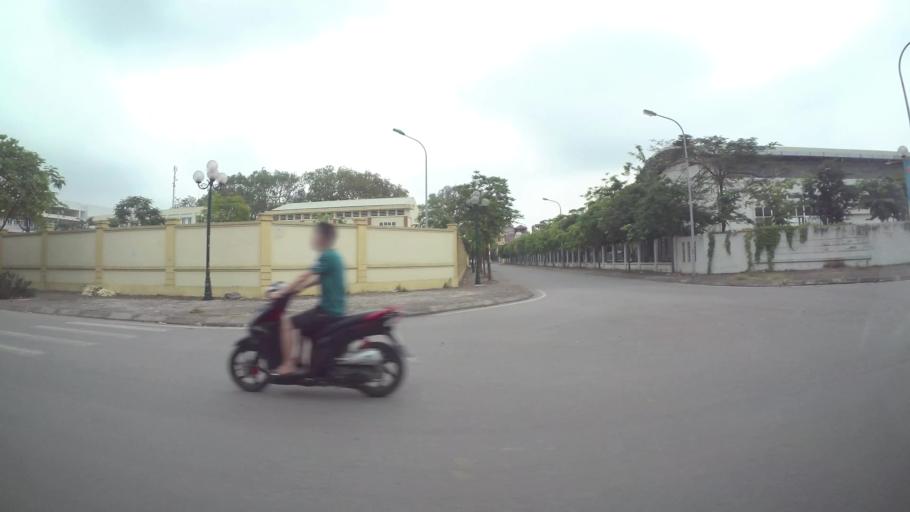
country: VN
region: Ha Noi
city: Trau Quy
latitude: 21.0478
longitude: 105.9248
